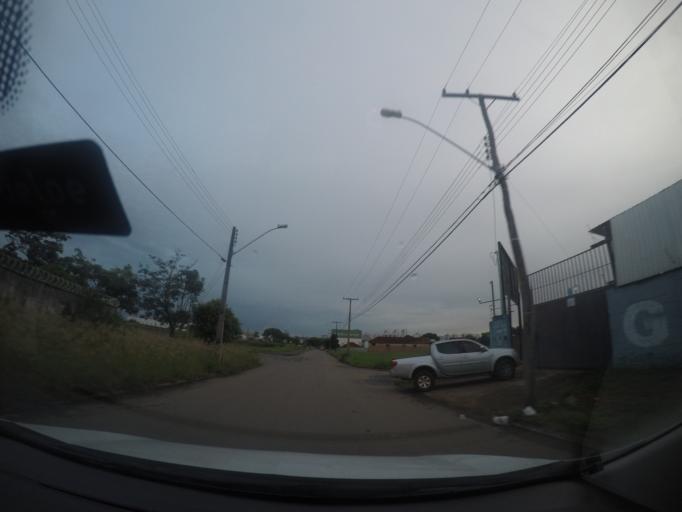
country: BR
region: Goias
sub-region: Goiania
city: Goiania
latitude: -16.6421
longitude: -49.2429
